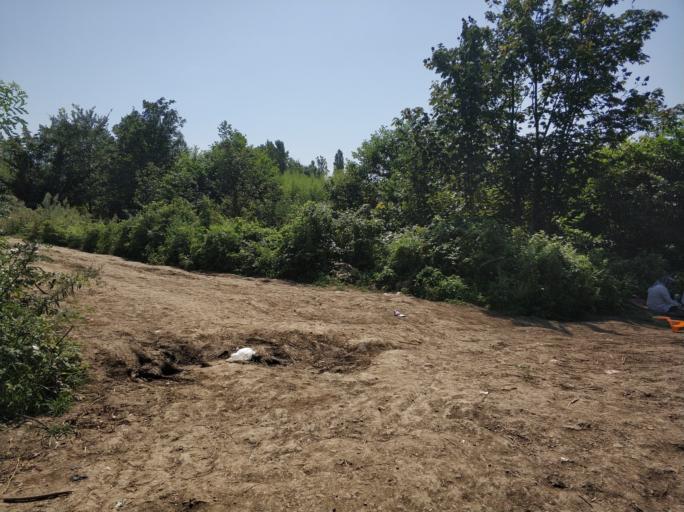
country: IR
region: Gilan
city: Lahijan
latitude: 37.1804
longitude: 50.0267
